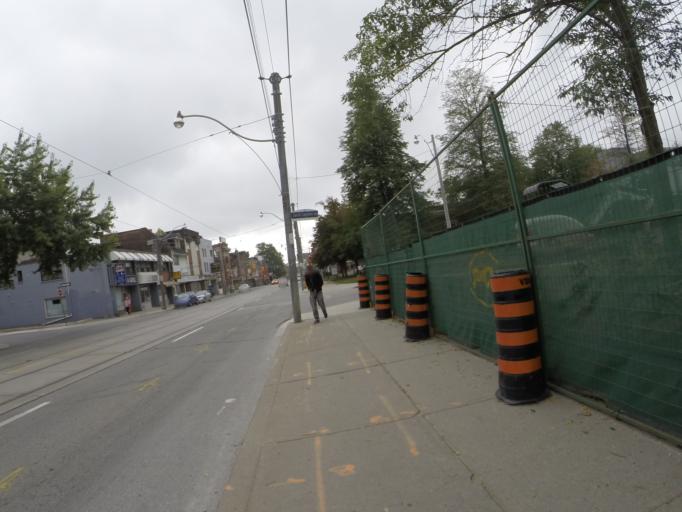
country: CA
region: Ontario
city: Toronto
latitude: 43.6676
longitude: -79.3536
